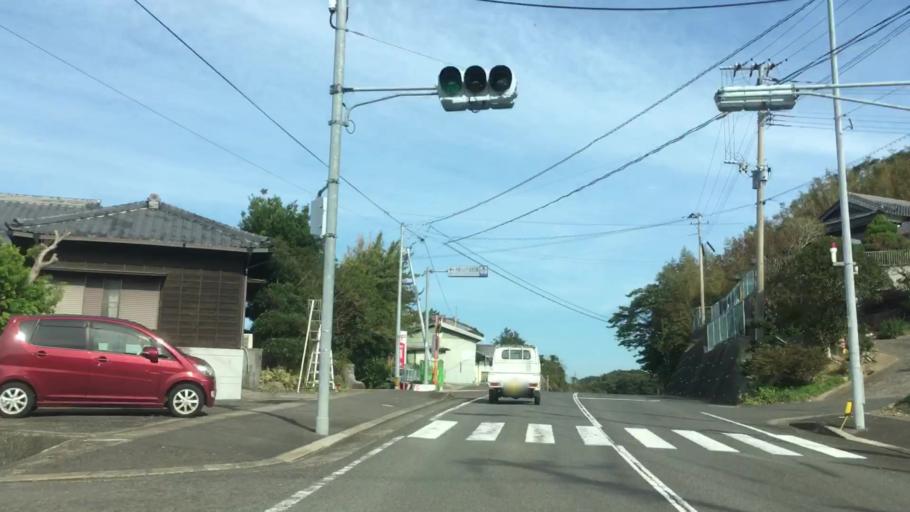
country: JP
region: Nagasaki
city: Sasebo
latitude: 33.0153
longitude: 129.6545
